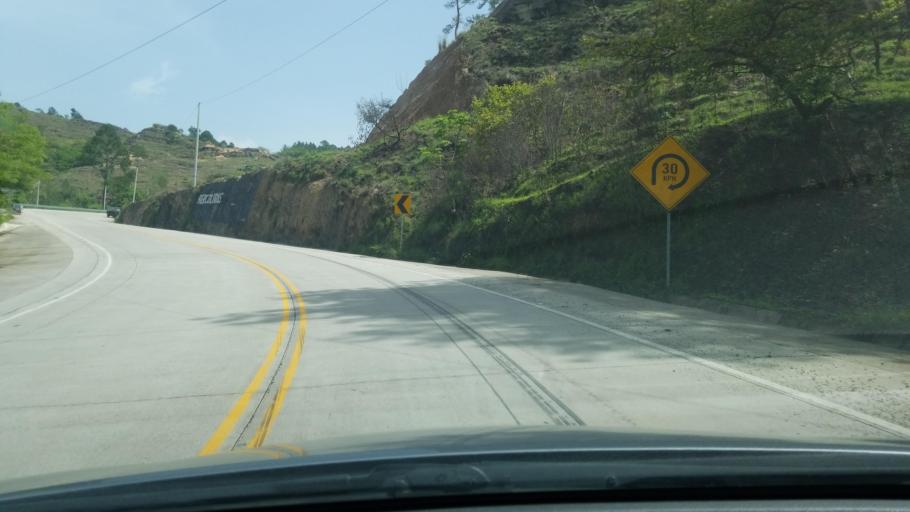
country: HN
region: Copan
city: Florida
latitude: 15.0136
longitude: -88.8341
